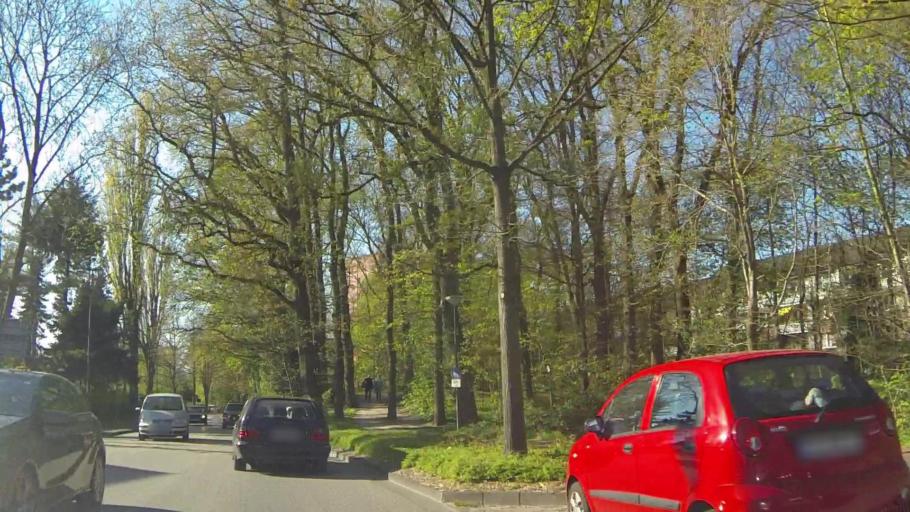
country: DE
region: Schleswig-Holstein
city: Wedel
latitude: 53.5828
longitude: 9.7134
